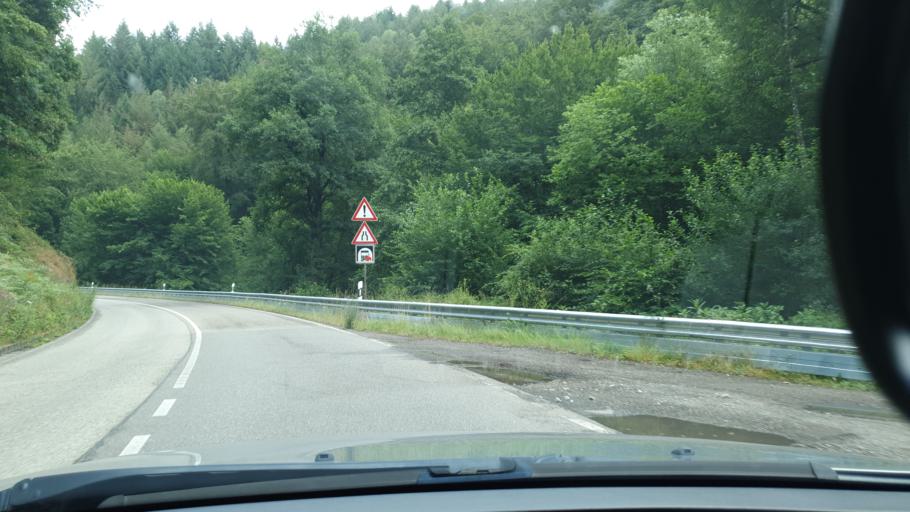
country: DE
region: Rheinland-Pfalz
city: Neidenfels
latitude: 49.3965
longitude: 8.0231
